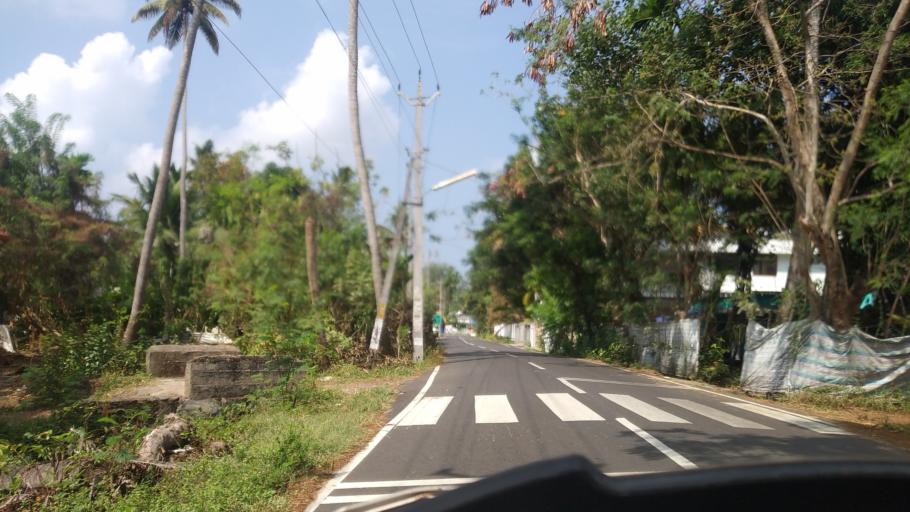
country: IN
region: Kerala
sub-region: Ernakulam
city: Elur
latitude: 10.1127
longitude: 76.2297
